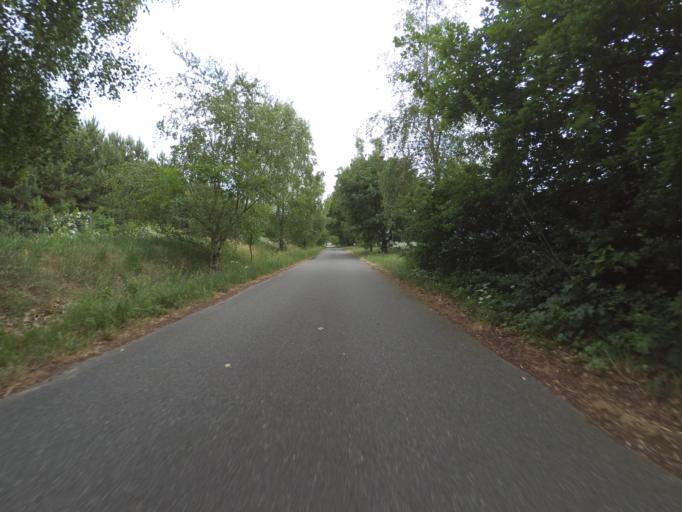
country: DE
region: Mecklenburg-Vorpommern
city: Grabowhofe
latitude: 53.5317
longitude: 12.5648
